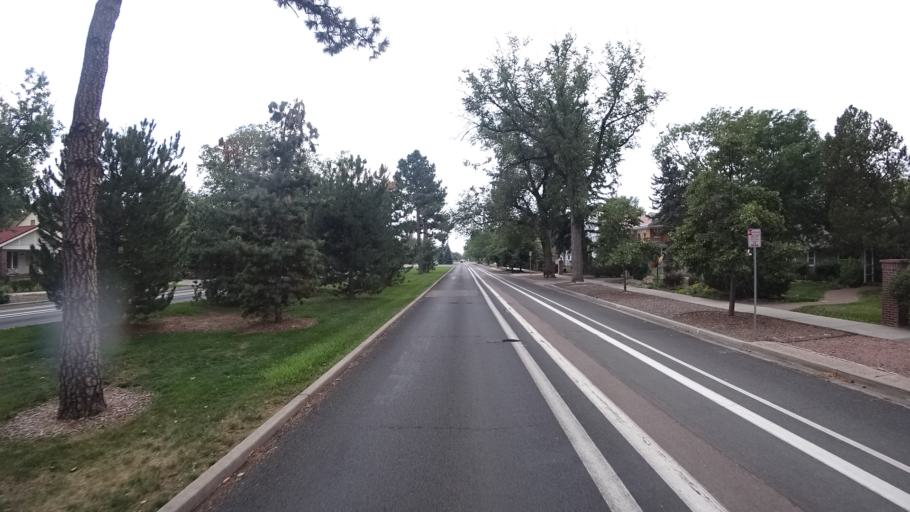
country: US
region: Colorado
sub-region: El Paso County
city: Colorado Springs
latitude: 38.8535
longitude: -104.8244
